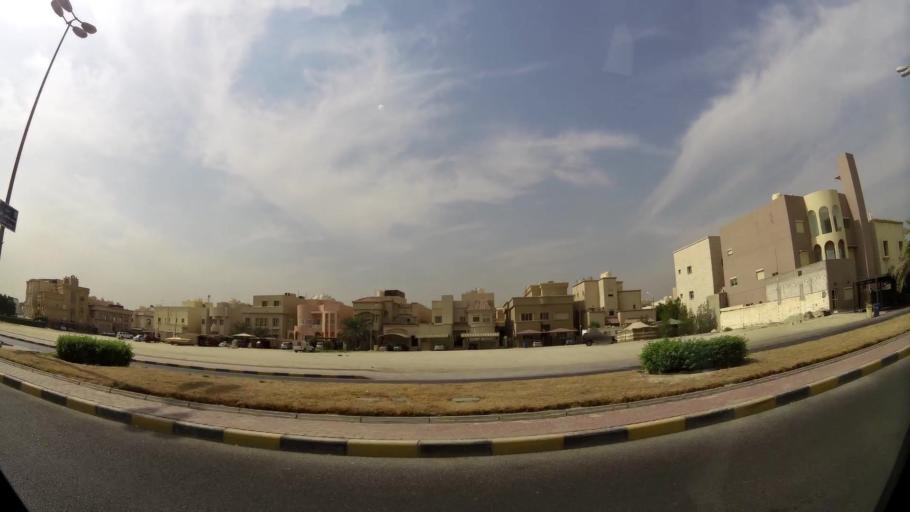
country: KW
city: Bayan
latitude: 29.2950
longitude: 48.0160
